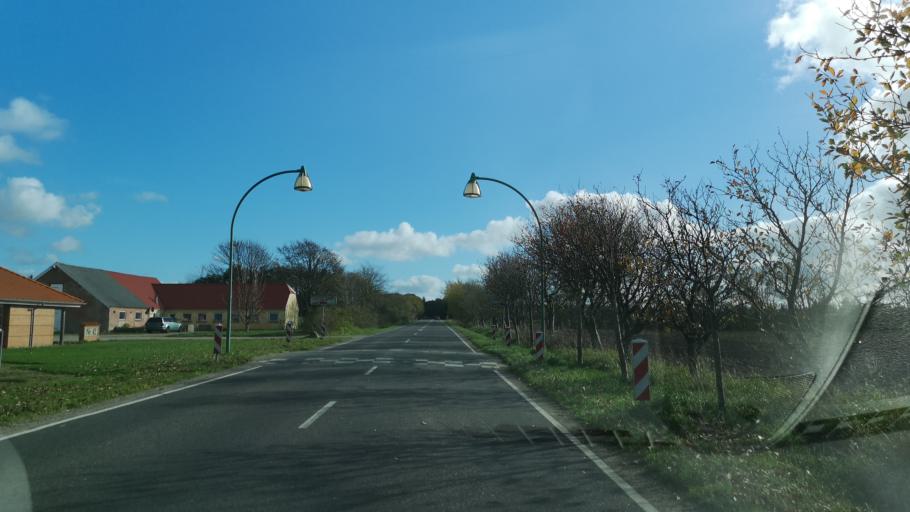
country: DK
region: South Denmark
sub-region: Varde Kommune
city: Oksbol
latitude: 55.7079
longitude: 8.3063
